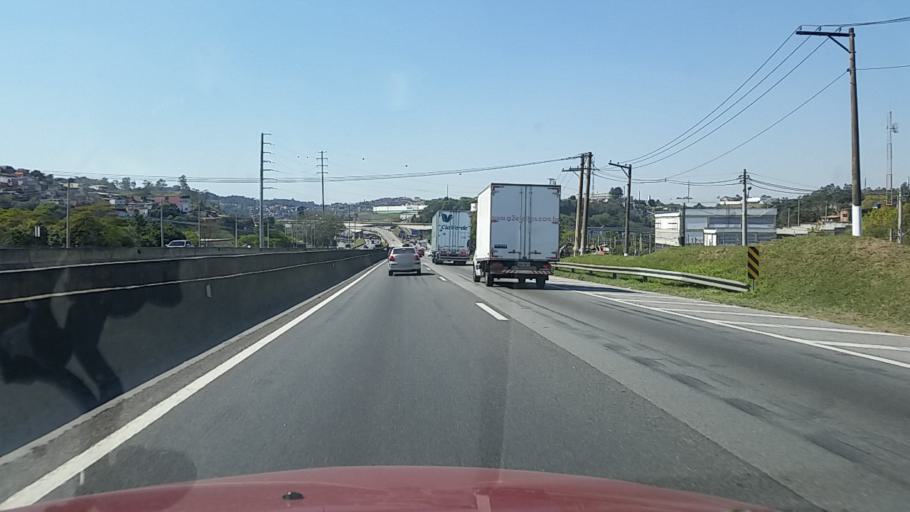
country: BR
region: Sao Paulo
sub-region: Embu
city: Embu
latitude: -23.6439
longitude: -46.8395
